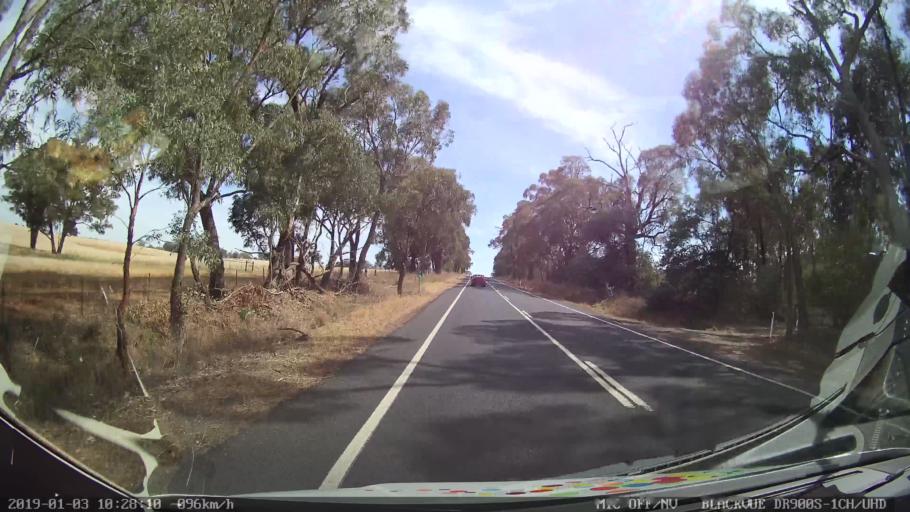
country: AU
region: New South Wales
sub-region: Young
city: Young
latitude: -34.3916
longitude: 148.2586
